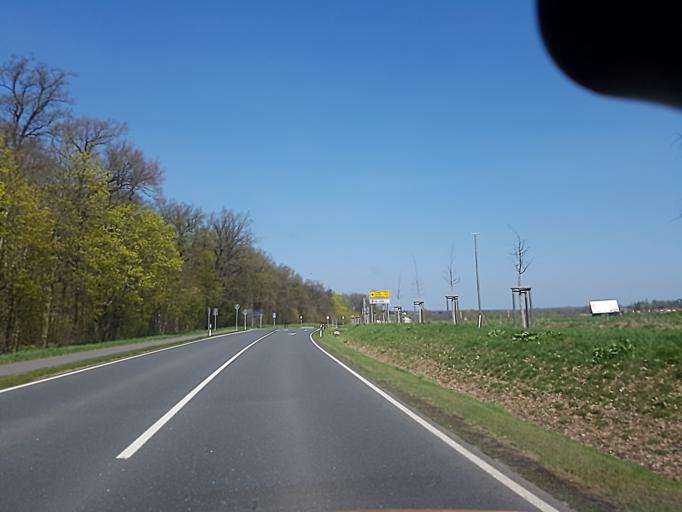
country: DE
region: Saxony
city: Mutzschen
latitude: 51.2685
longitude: 12.9208
